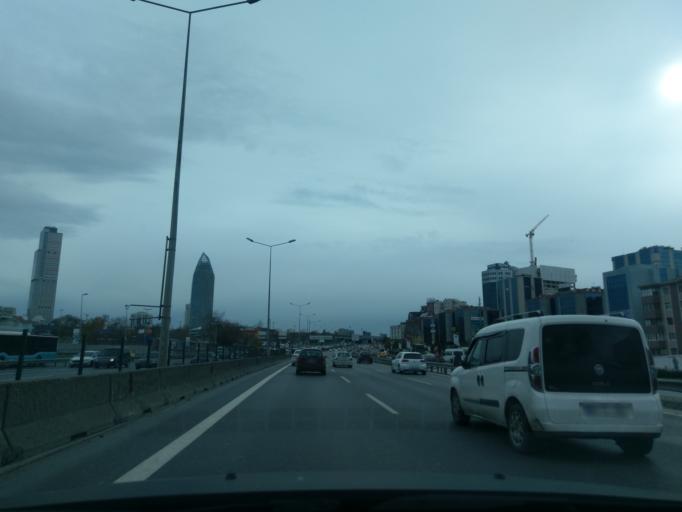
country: TR
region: Istanbul
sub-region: Atasehir
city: Atasehir
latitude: 40.9861
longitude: 29.0890
